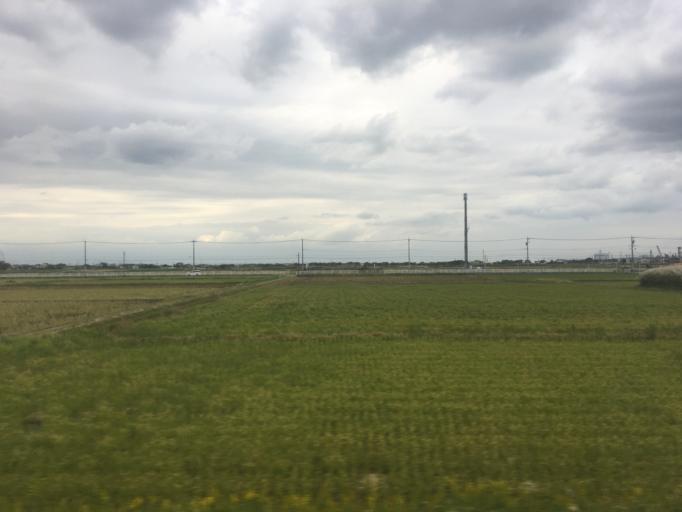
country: JP
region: Chiba
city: Kisarazu
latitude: 35.4296
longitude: 139.9506
